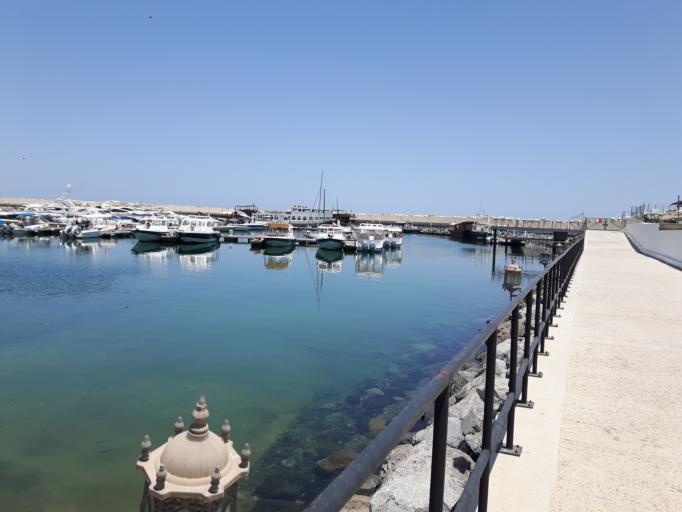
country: OM
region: Muhafazat Masqat
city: Muscat
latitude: 23.5813
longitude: 58.6064
